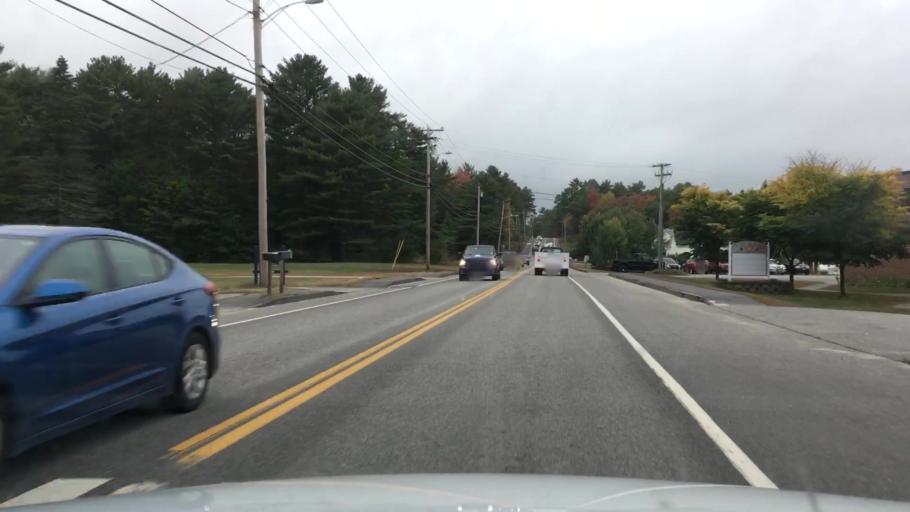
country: US
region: Maine
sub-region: Androscoggin County
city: Poland
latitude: 44.0636
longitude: -70.3971
